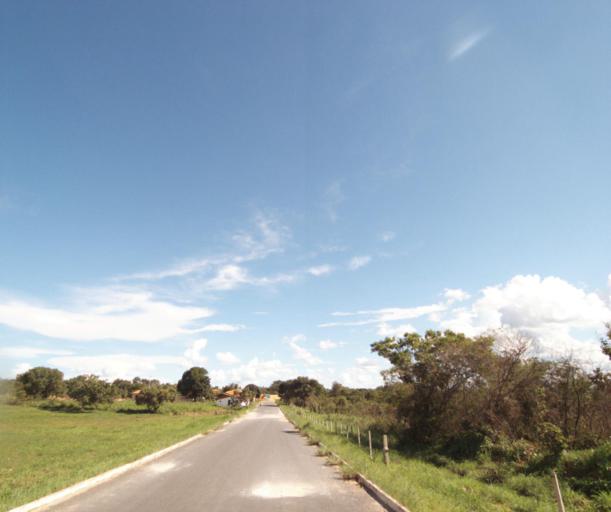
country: BR
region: Bahia
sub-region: Correntina
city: Correntina
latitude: -13.3200
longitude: -44.6369
